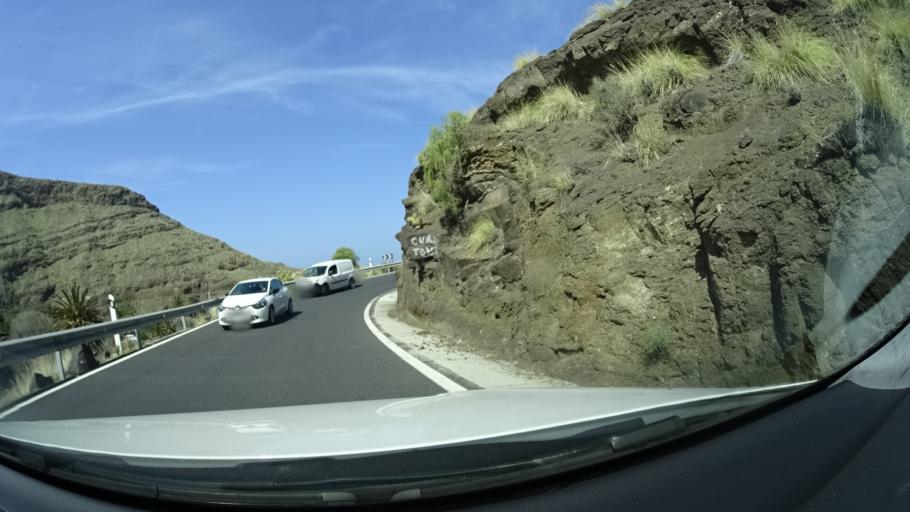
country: ES
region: Canary Islands
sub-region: Provincia de Las Palmas
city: Agaete
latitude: 28.0818
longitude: -15.7054
